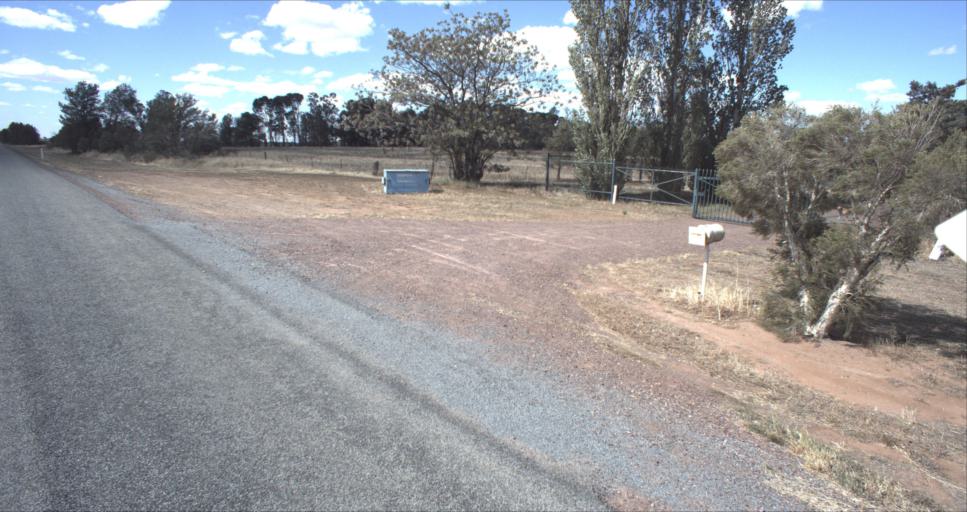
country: AU
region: New South Wales
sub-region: Leeton
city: Leeton
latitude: -34.4846
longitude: 146.2484
